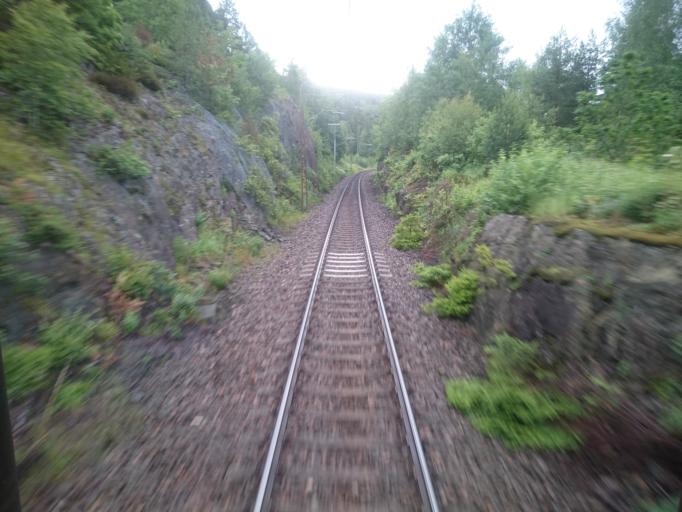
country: SE
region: OEstergoetland
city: Lindo
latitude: 58.6687
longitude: 16.2775
